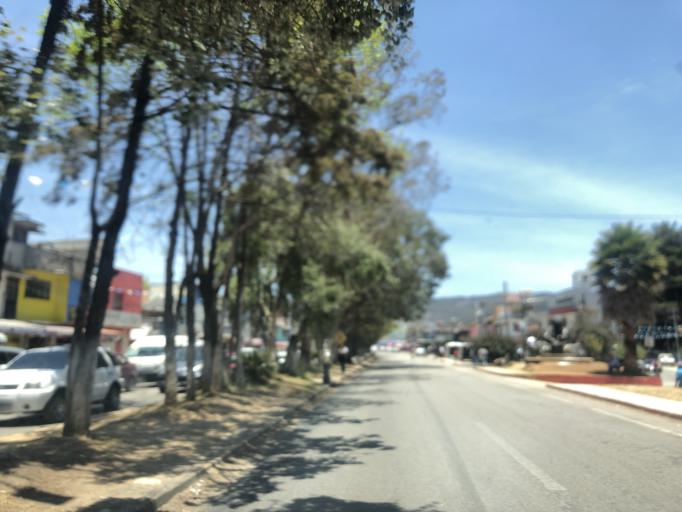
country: MX
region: Chiapas
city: San Cristobal de las Casas
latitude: 16.7273
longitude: -92.6359
